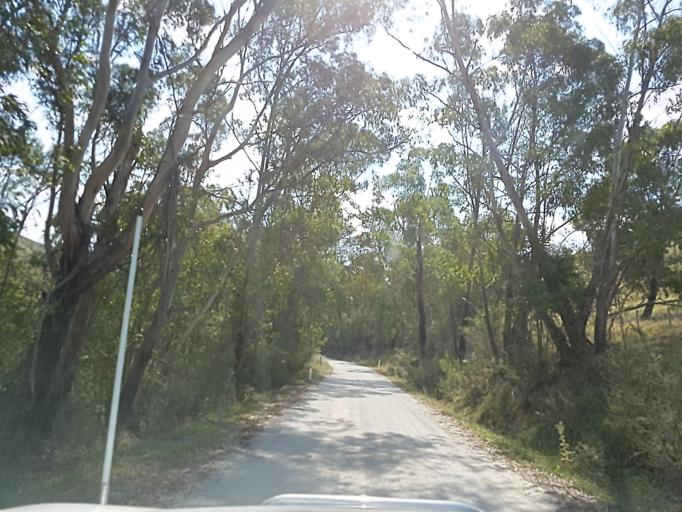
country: AU
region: Victoria
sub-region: East Gippsland
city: Lakes Entrance
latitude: -37.4926
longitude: 148.2291
